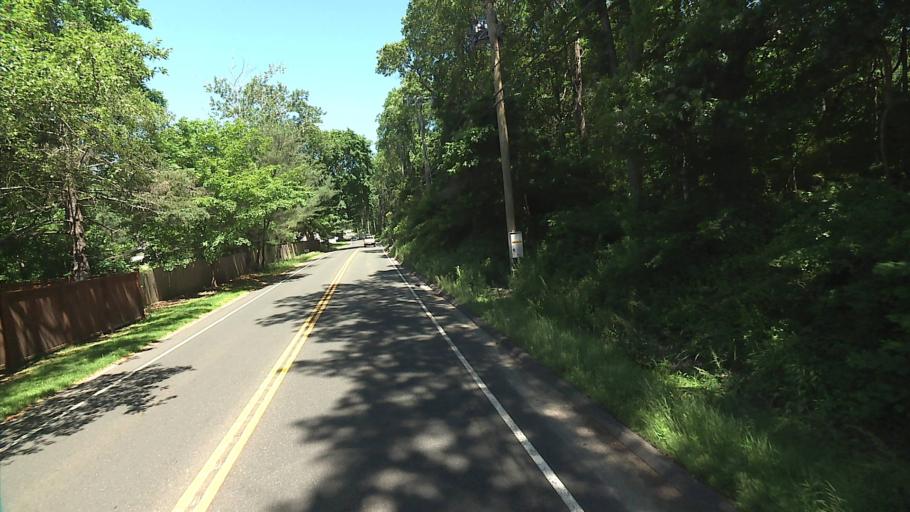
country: US
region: Connecticut
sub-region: New Haven County
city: Guilford
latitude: 41.3146
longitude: -72.6955
